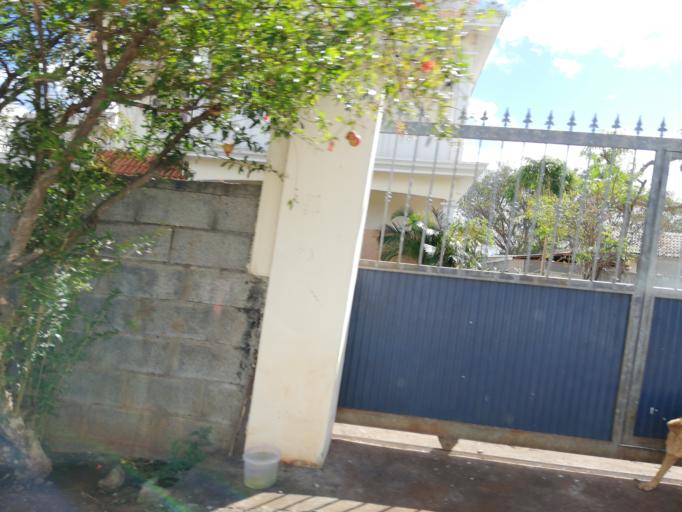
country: MU
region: Black River
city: Petite Riviere
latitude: -20.1942
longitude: 57.4631
